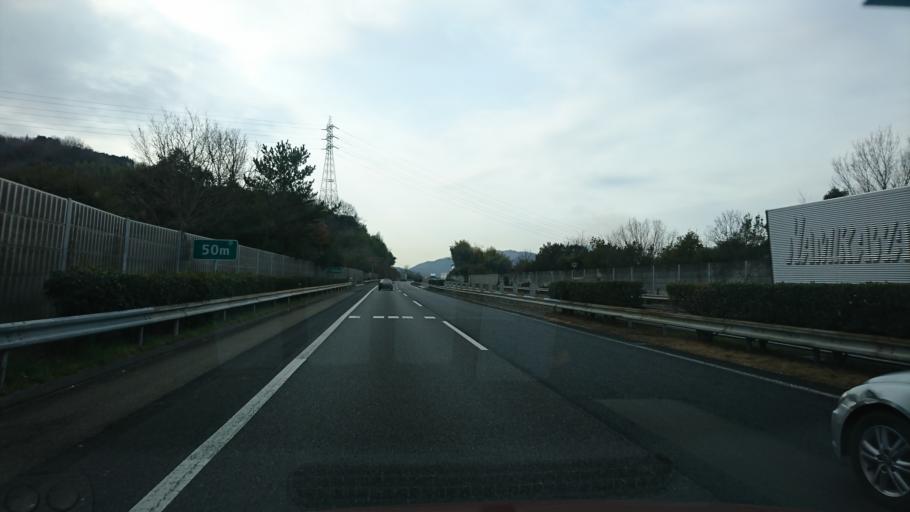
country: JP
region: Okayama
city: Kamogatacho-kamogata
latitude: 34.5451
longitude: 133.5690
